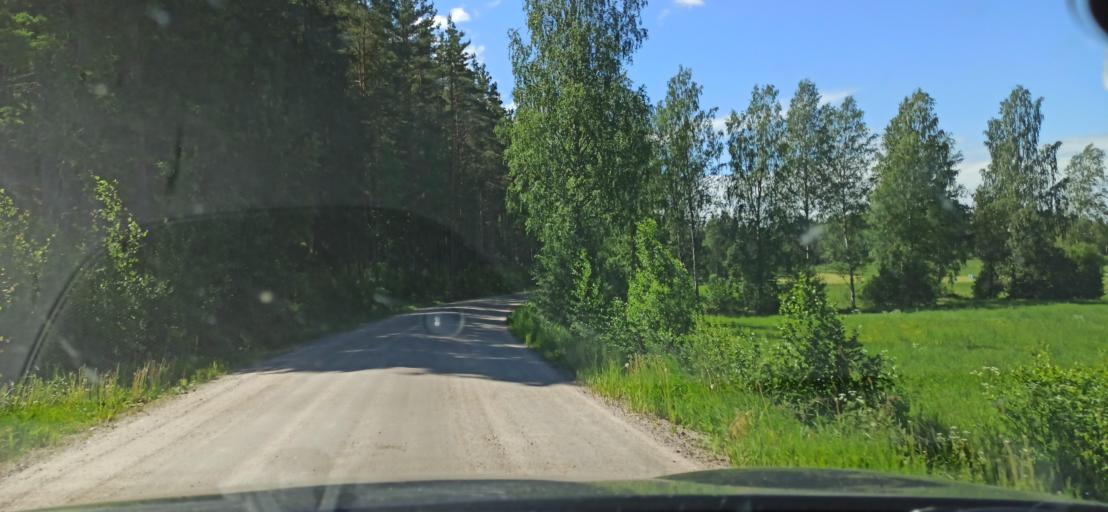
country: FI
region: Varsinais-Suomi
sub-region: Turku
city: Sauvo
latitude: 60.3835
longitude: 22.6482
